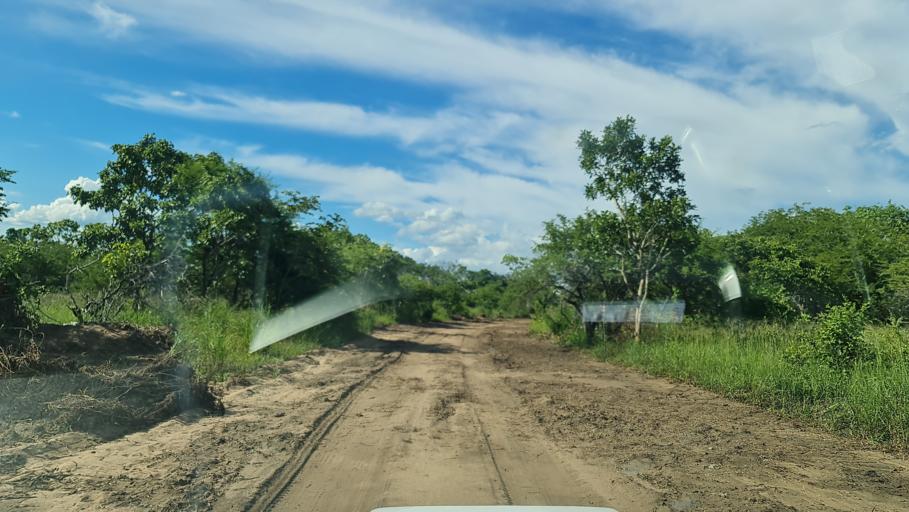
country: MZ
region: Nampula
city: Antonio Enes
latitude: -15.5260
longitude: 40.1269
